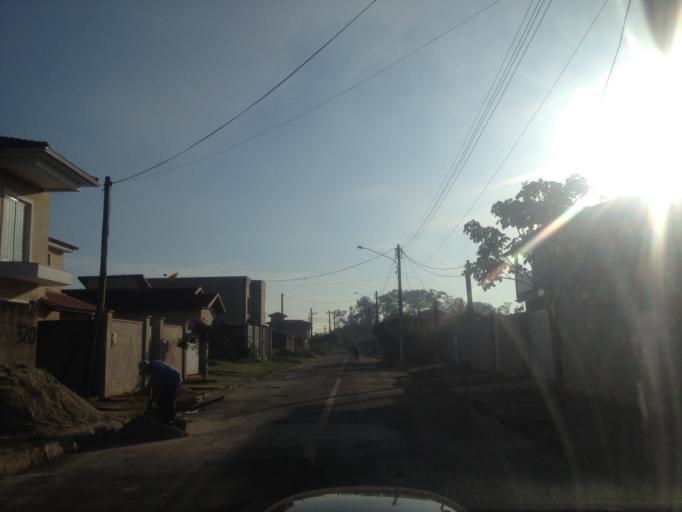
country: BR
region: Rio de Janeiro
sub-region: Porto Real
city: Porto Real
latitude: -22.4123
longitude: -44.3119
